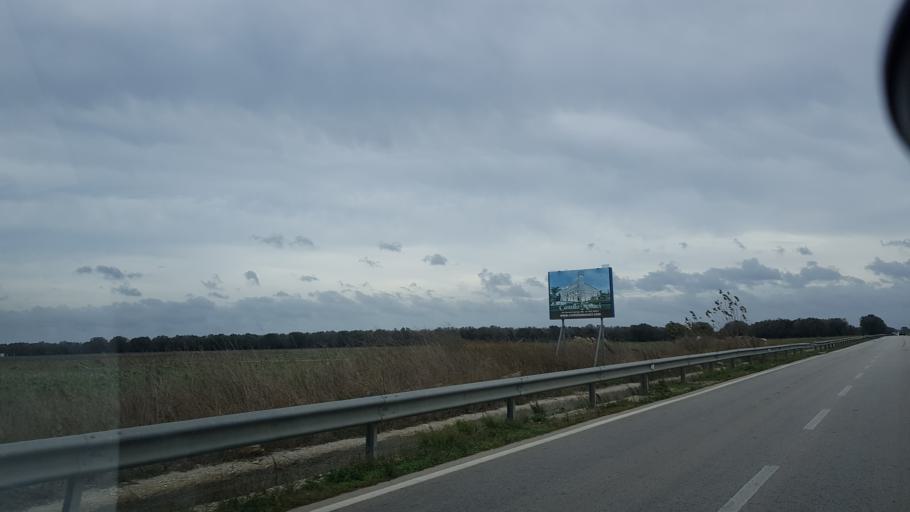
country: IT
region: Apulia
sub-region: Provincia di Brindisi
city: San Pancrazio Salentino
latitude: 40.4090
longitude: 17.8774
